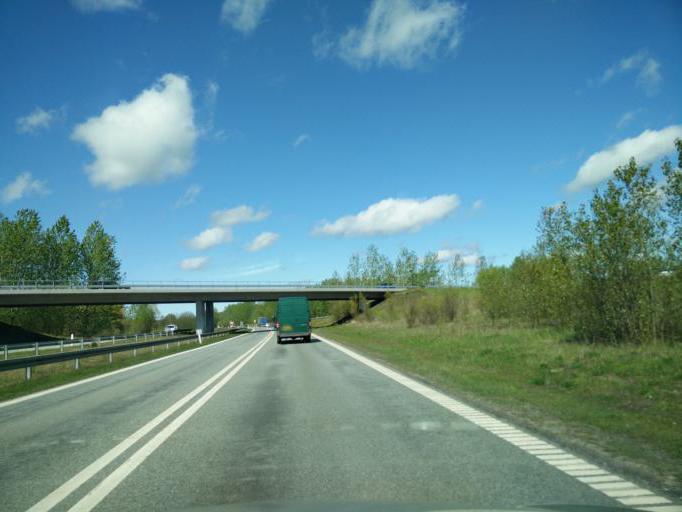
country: DK
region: Capital Region
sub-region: Hillerod Kommune
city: Hillerod
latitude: 55.9541
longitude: 12.2458
